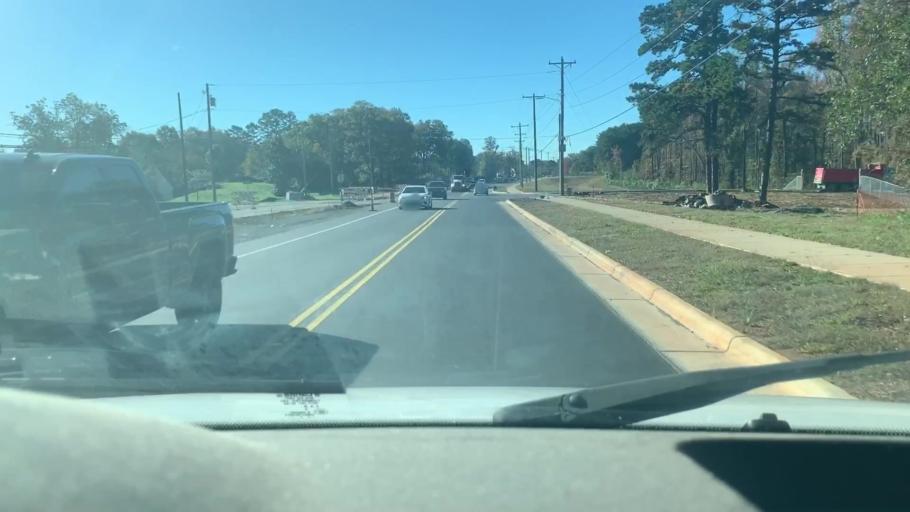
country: US
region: North Carolina
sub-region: Mecklenburg County
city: Charlotte
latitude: 35.2957
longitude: -80.8564
